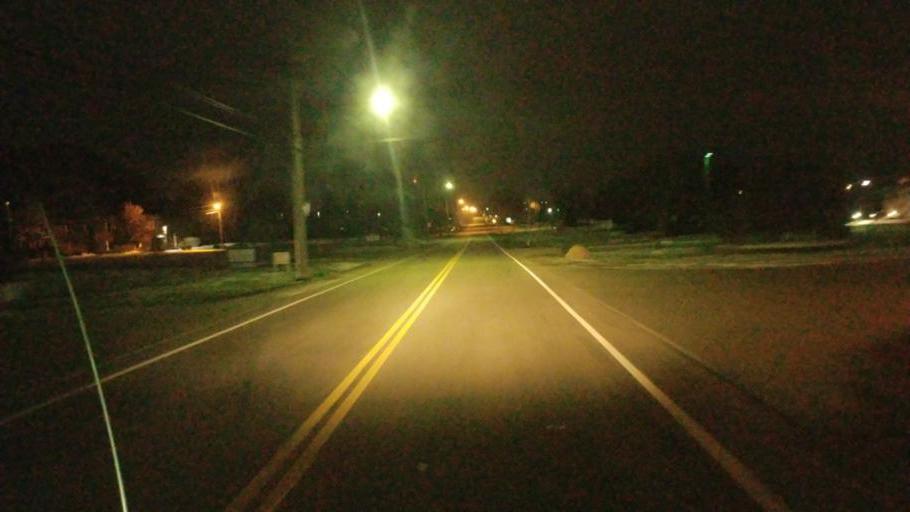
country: US
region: Ohio
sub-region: Cuyahoga County
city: Solon
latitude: 41.3872
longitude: -81.4615
